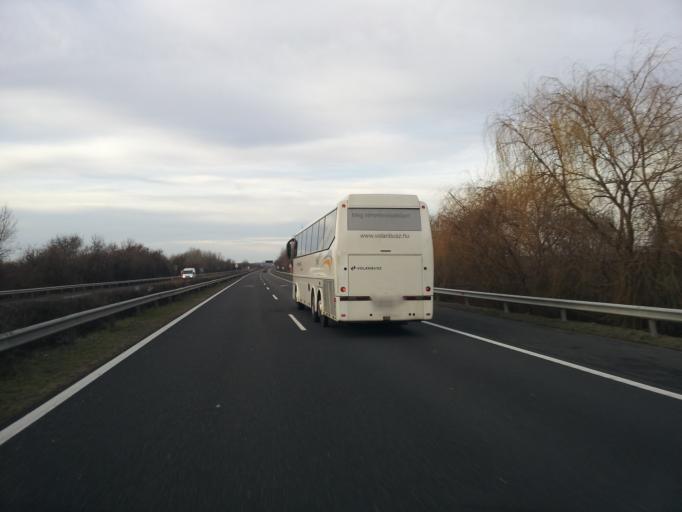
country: HU
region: Fejer
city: Lepseny
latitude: 47.0097
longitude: 18.2347
